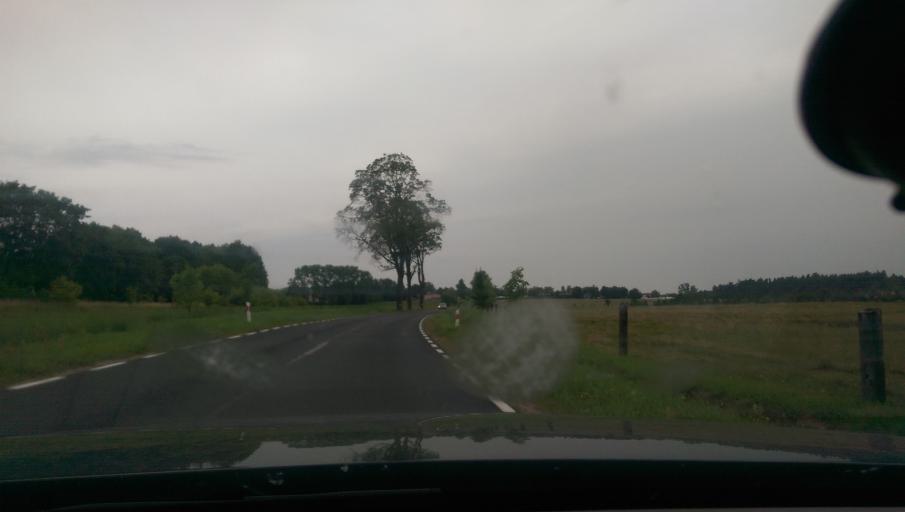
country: PL
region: Warmian-Masurian Voivodeship
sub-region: Powiat piski
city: Orzysz
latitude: 53.8103
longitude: 21.8494
